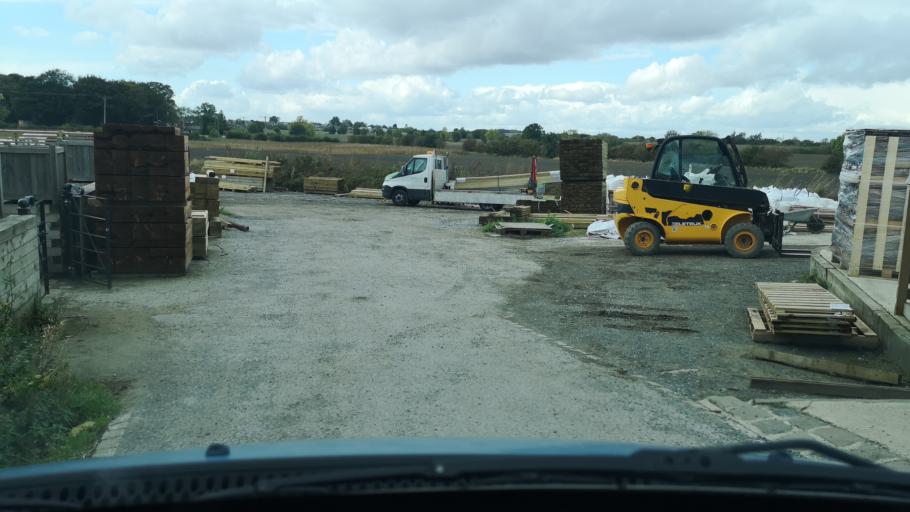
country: GB
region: England
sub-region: City and Borough of Wakefield
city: Featherstone
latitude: 53.6807
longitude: -1.3356
